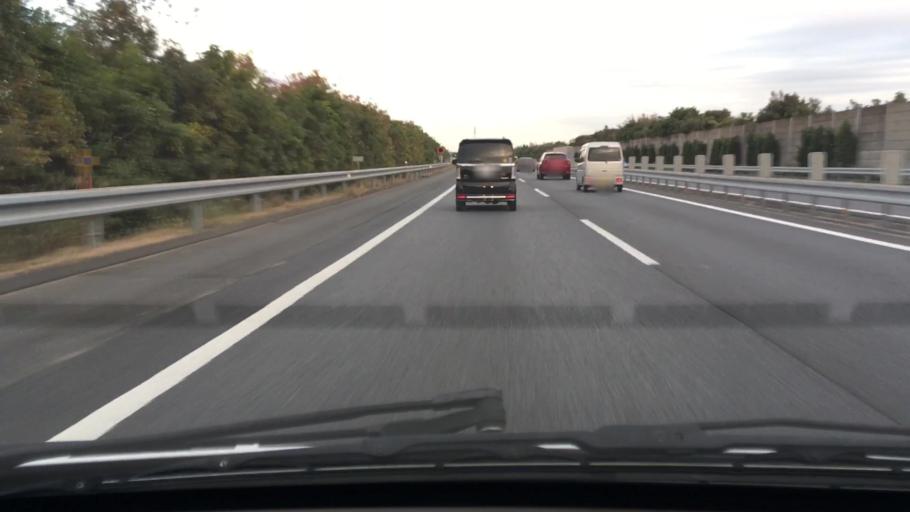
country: JP
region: Chiba
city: Ichihara
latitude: 35.5155
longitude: 140.1178
